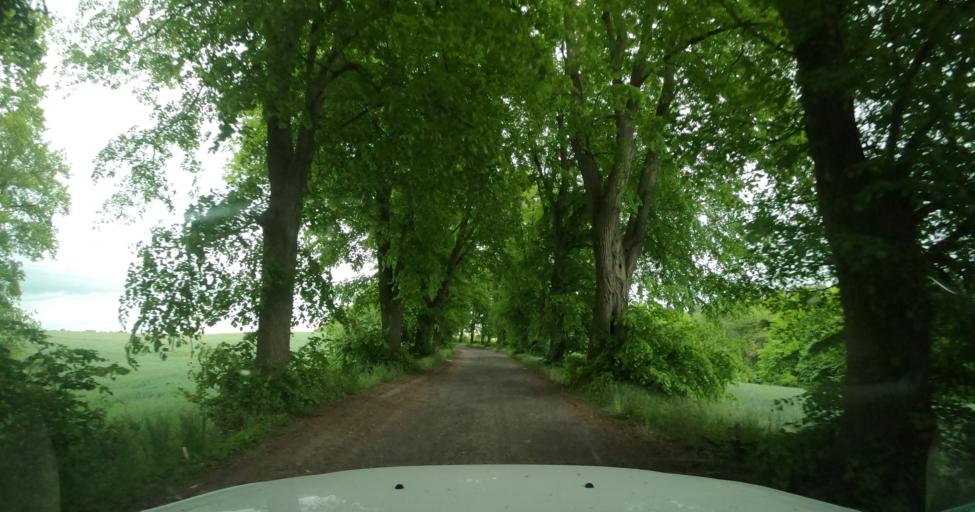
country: PL
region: West Pomeranian Voivodeship
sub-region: Powiat stargardzki
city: Dolice
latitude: 53.2439
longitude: 15.2475
